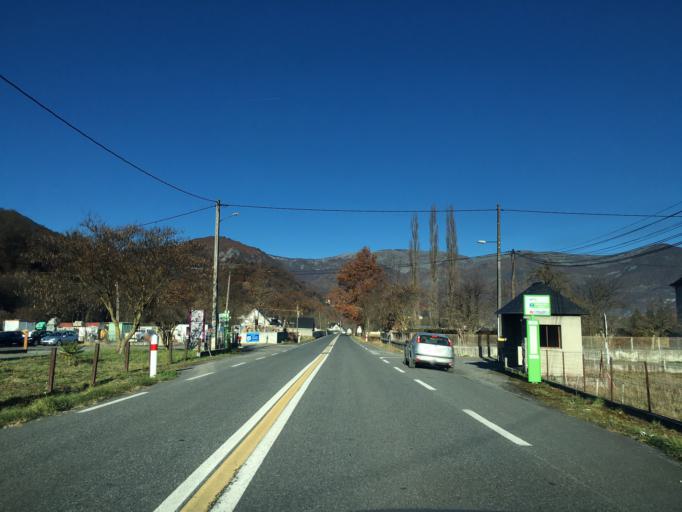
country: FR
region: Midi-Pyrenees
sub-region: Departement des Hautes-Pyrenees
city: Pierrefitte-Nestalas
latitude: 42.9810
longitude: -0.0843
